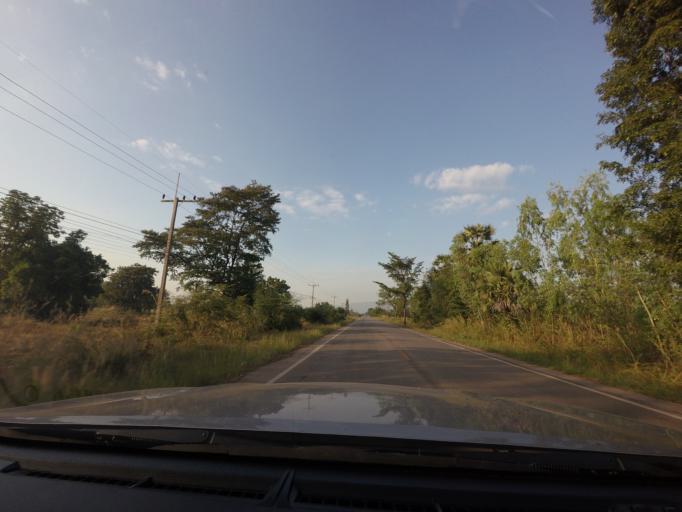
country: TH
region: Phitsanulok
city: Noen Maprang
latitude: 16.6285
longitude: 100.6182
